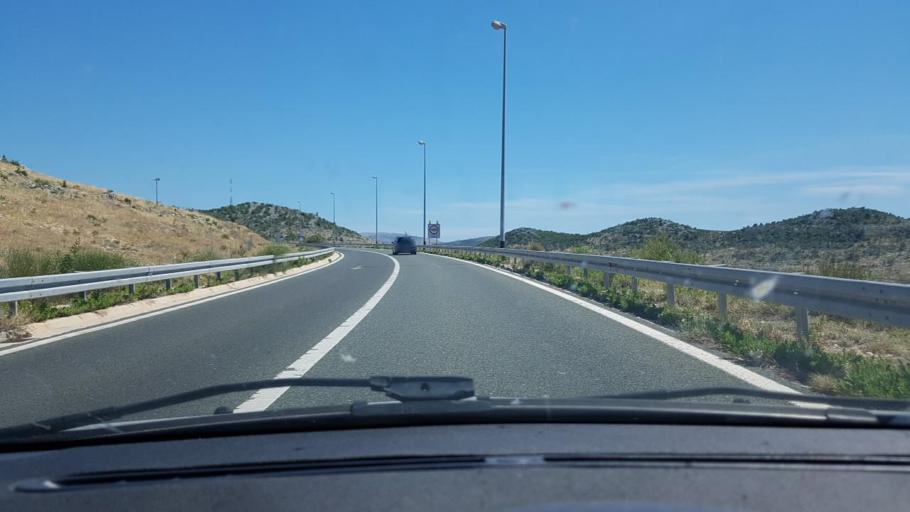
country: HR
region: Sibensko-Kniniska
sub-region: Grad Sibenik
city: Sibenik
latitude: 43.7610
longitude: 15.9308
